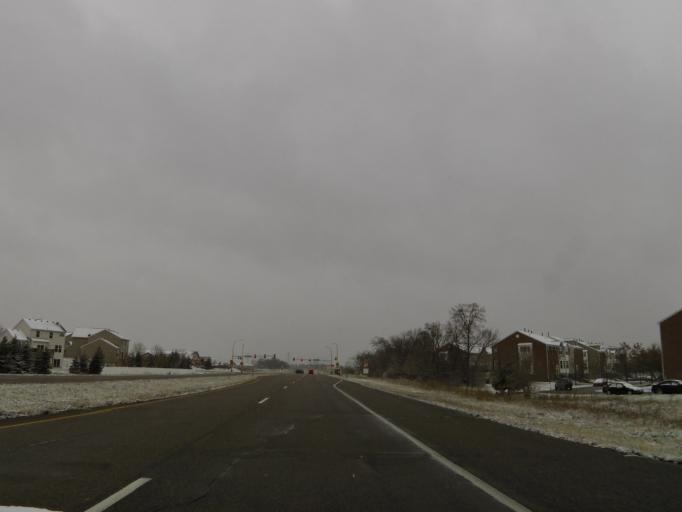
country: US
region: Minnesota
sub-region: Scott County
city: Prior Lake
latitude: 44.7701
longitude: -93.4096
